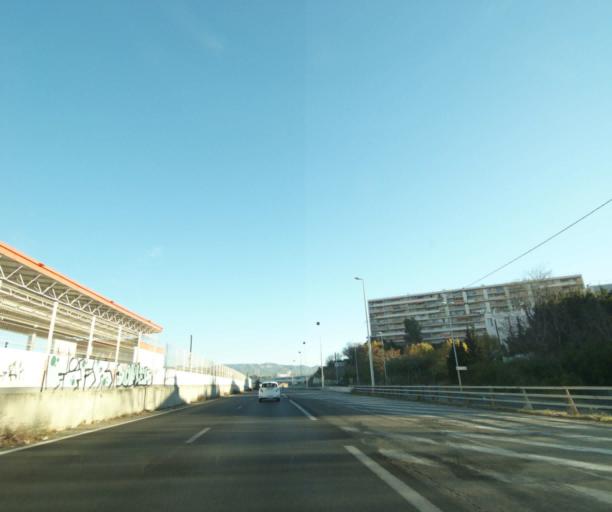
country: FR
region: Provence-Alpes-Cote d'Azur
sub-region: Departement des Bouches-du-Rhone
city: Marseille 13
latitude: 43.3209
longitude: 5.4166
